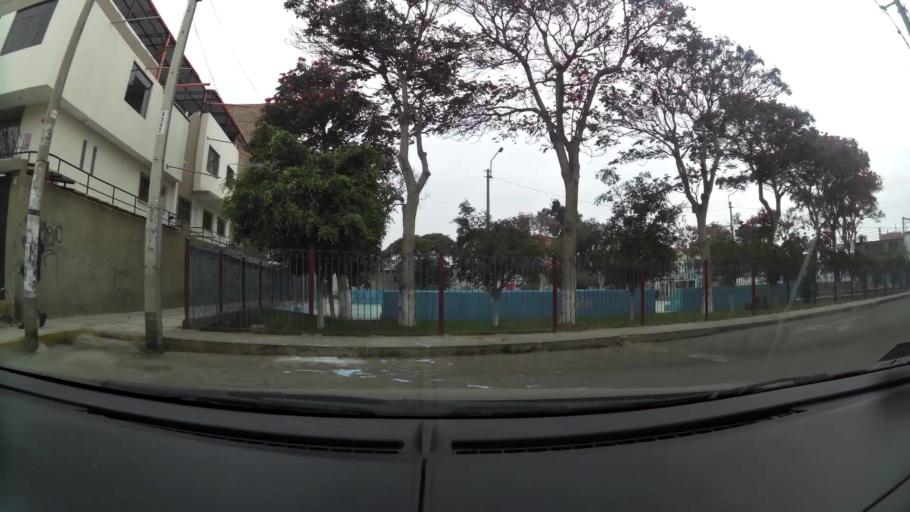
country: PE
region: La Libertad
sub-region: Provincia de Trujillo
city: Trujillo
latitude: -8.1051
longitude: -79.0419
